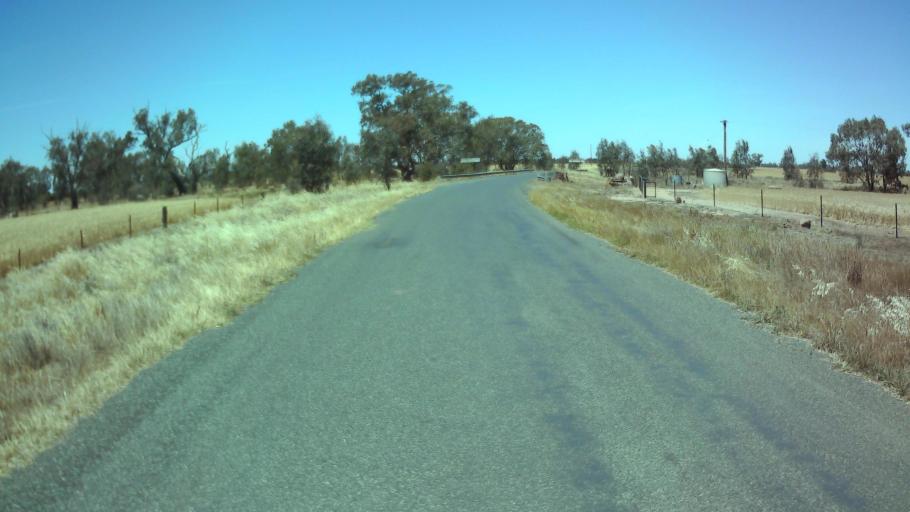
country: AU
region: New South Wales
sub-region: Weddin
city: Grenfell
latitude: -34.0380
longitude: 147.7898
